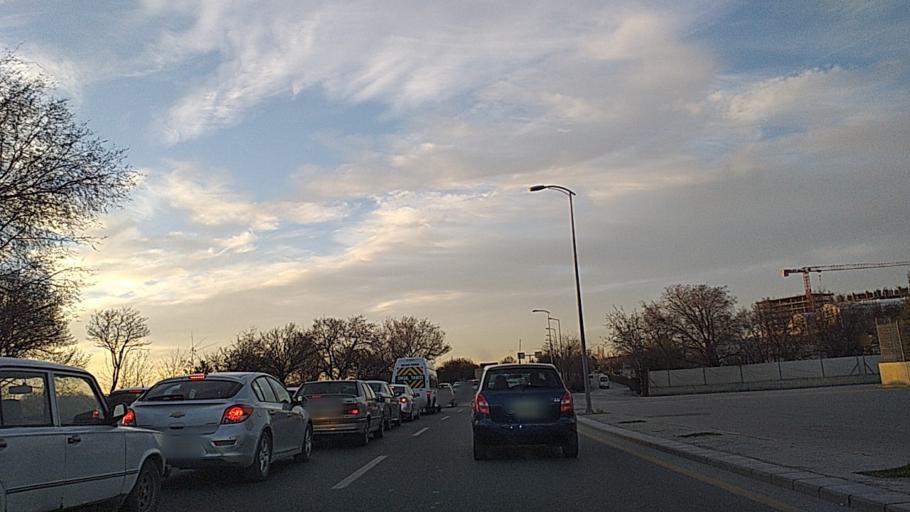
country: TR
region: Ankara
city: Batikent
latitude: 39.9601
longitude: 32.6868
